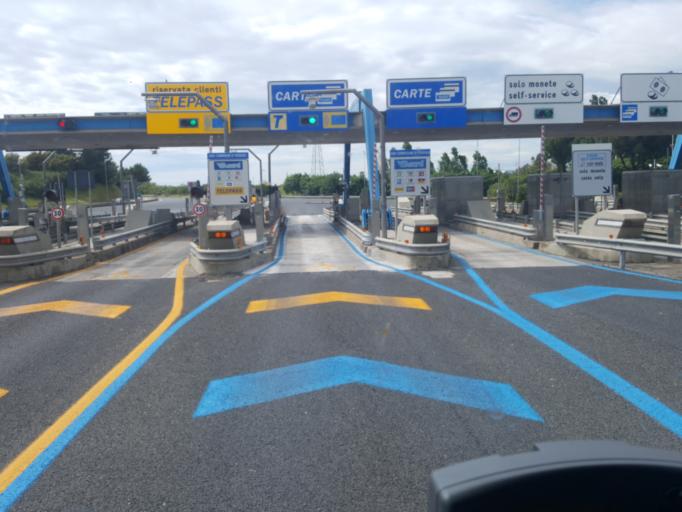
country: IT
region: Latium
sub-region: Citta metropolitana di Roma Capitale
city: Ara Nova
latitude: 41.9158
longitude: 12.2114
